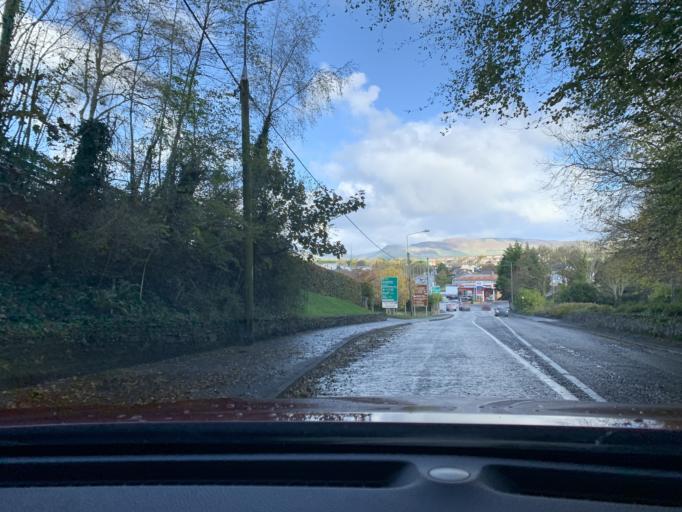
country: IE
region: Connaught
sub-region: Sligo
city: Sligo
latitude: 54.2752
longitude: -8.4602
